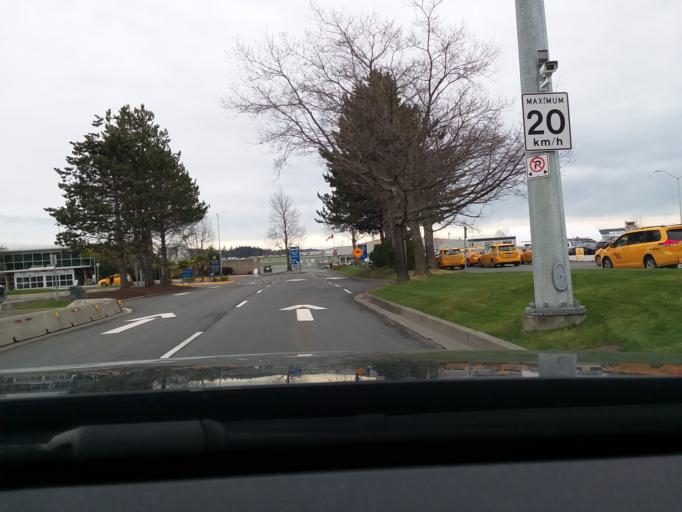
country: CA
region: British Columbia
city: North Saanich
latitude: 48.6392
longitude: -123.4289
